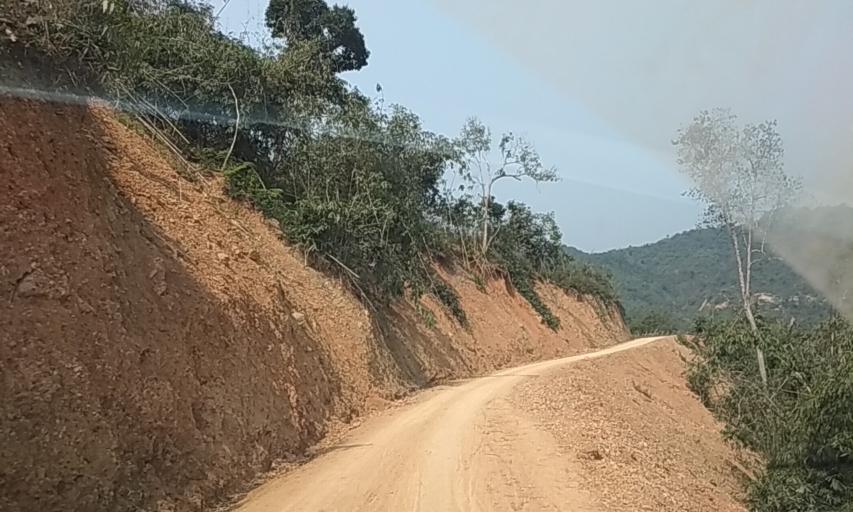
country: LA
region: Phongsali
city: Phongsali
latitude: 21.4764
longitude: 102.4367
